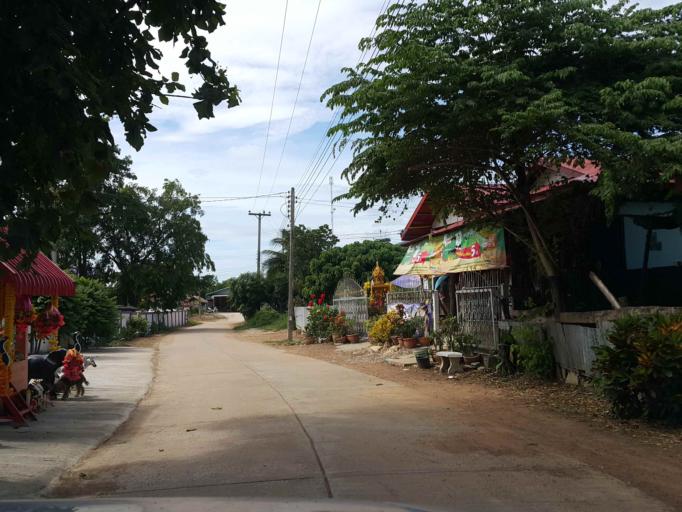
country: TH
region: Sukhothai
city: Ban Dan Lan Hoi
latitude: 17.1046
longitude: 99.4753
